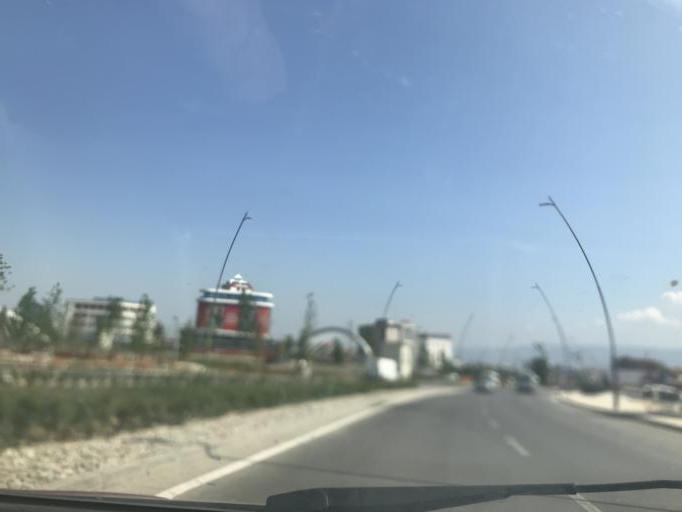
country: TR
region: Denizli
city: Denizli
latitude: 37.7822
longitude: 29.0973
